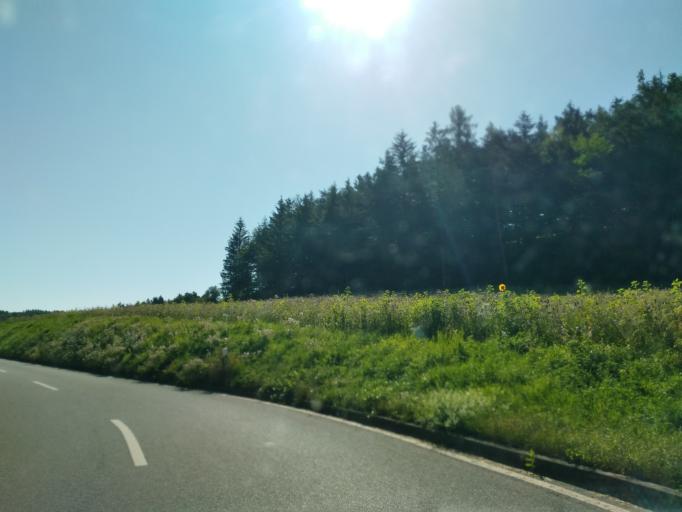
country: DE
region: Baden-Wuerttemberg
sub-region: Karlsruhe Region
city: Buchen
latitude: 49.5151
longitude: 9.2834
